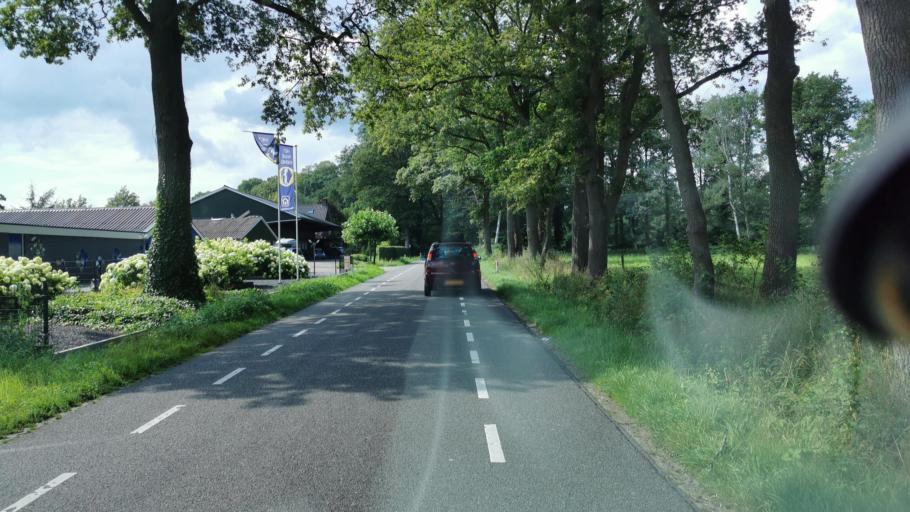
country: NL
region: Overijssel
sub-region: Gemeente Enschede
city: Enschede
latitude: 52.2280
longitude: 6.9295
